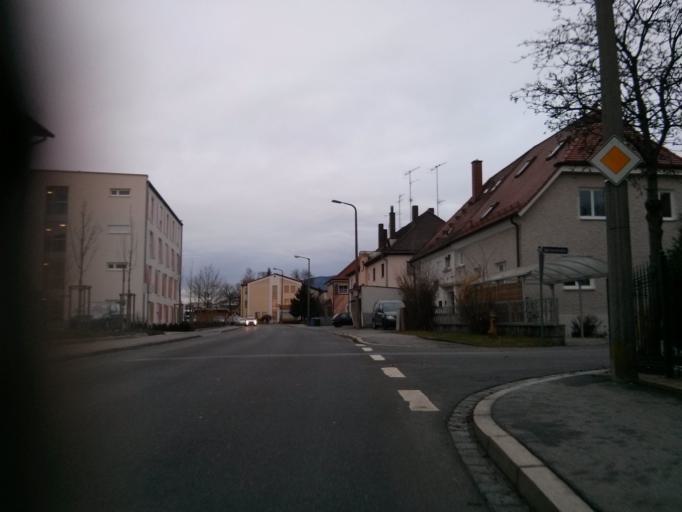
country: DE
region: Bavaria
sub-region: Lower Bavaria
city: Deggendorf
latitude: 48.8369
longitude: 12.9494
